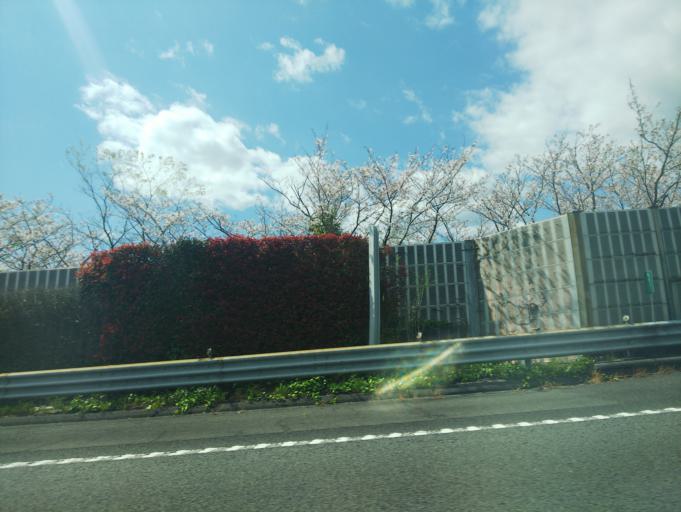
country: JP
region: Shizuoka
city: Shizuoka-shi
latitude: 35.0100
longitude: 138.4345
